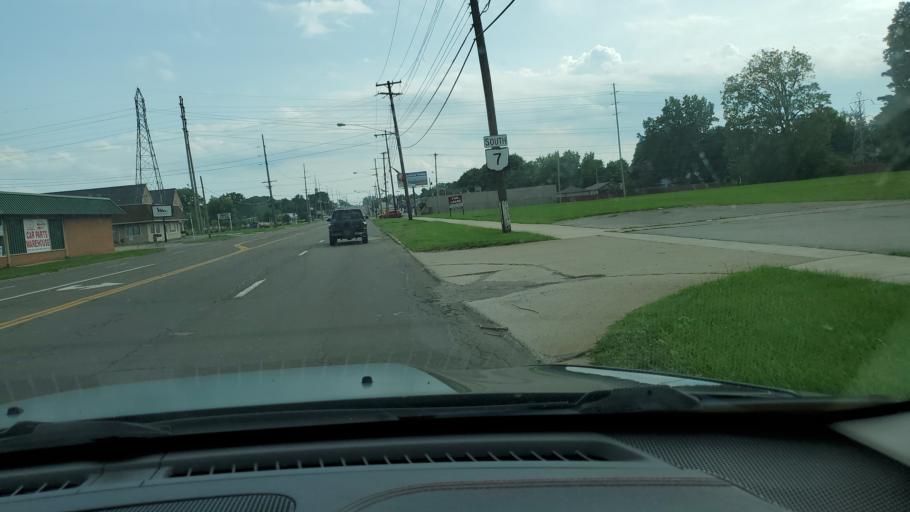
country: US
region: Ohio
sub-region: Mahoning County
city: Boardman
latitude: 41.0348
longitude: -80.6629
